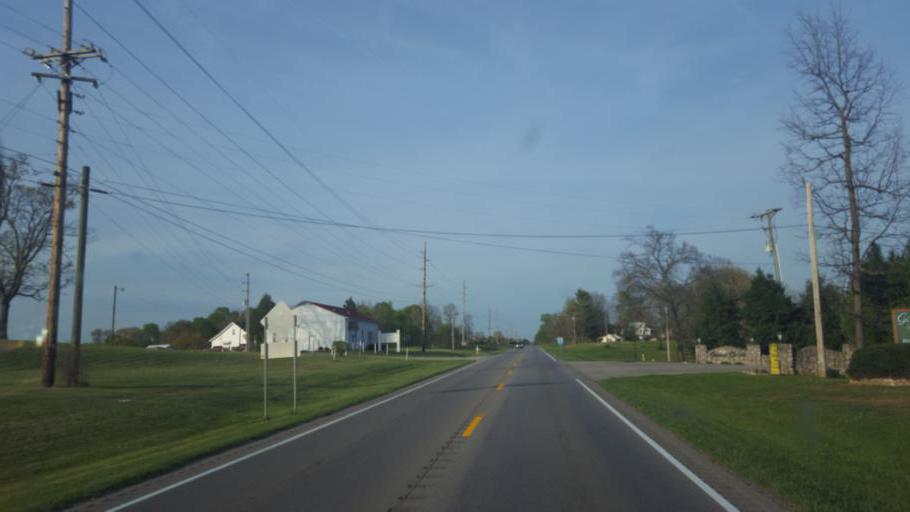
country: US
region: Kentucky
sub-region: Barren County
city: Glasgow
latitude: 36.9547
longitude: -85.9613
